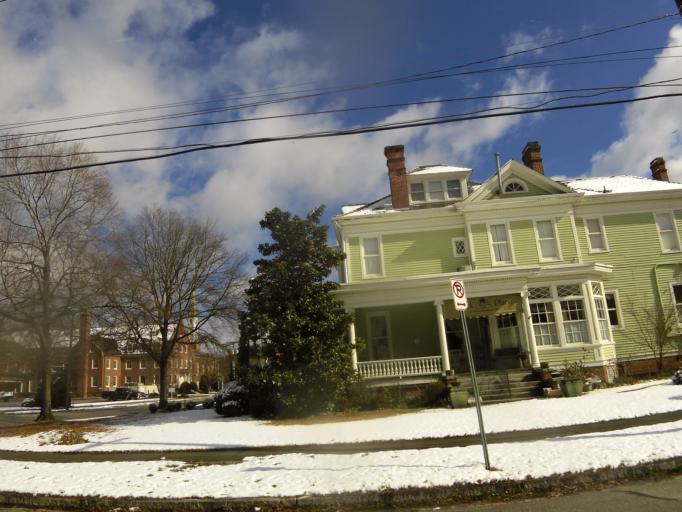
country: US
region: North Carolina
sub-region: Wilson County
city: Wilson
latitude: 35.7286
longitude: -77.9159
